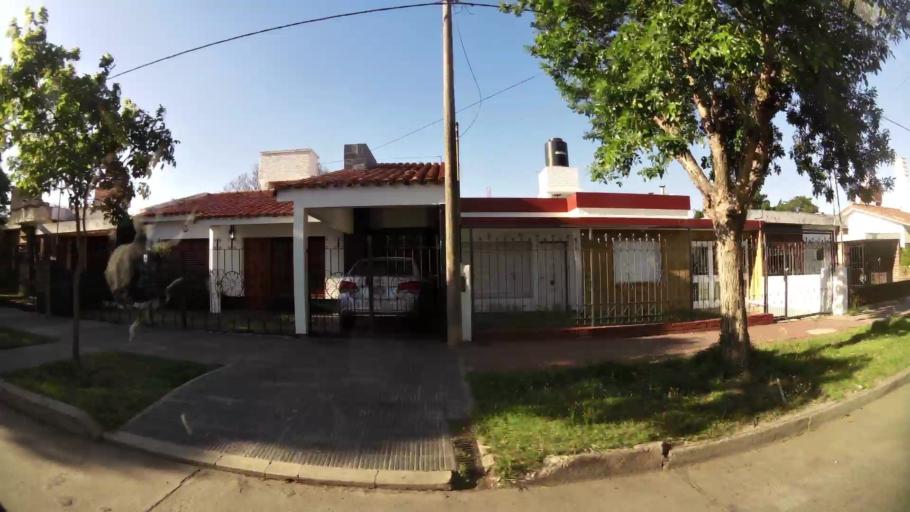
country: AR
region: Cordoba
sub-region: Departamento de Capital
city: Cordoba
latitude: -31.3767
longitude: -64.1777
